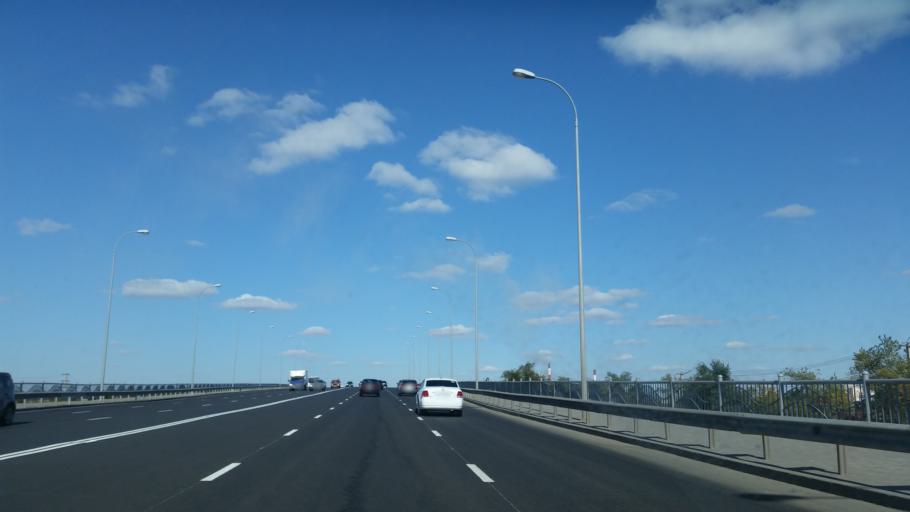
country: KZ
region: Astana Qalasy
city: Astana
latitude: 51.1695
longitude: 71.4796
